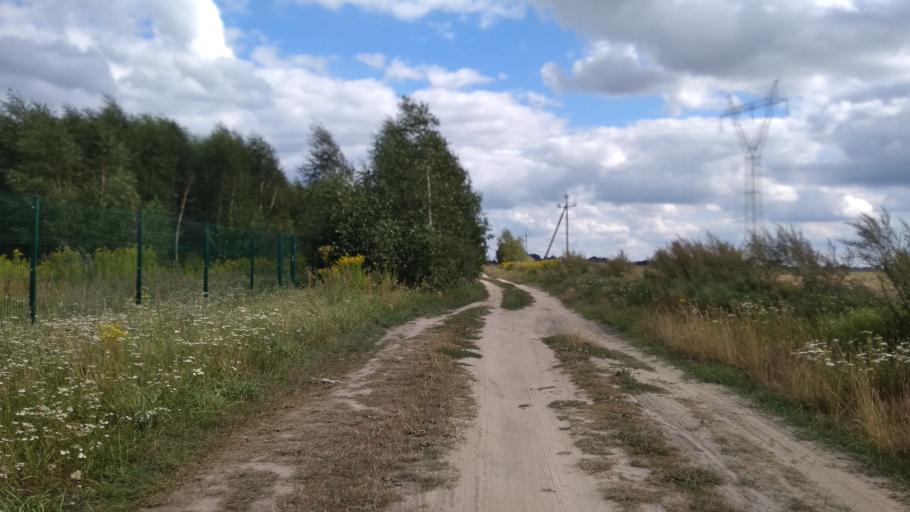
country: PL
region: Kujawsko-Pomorskie
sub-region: Powiat bydgoski
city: Osielsko
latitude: 53.2221
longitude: 18.1409
